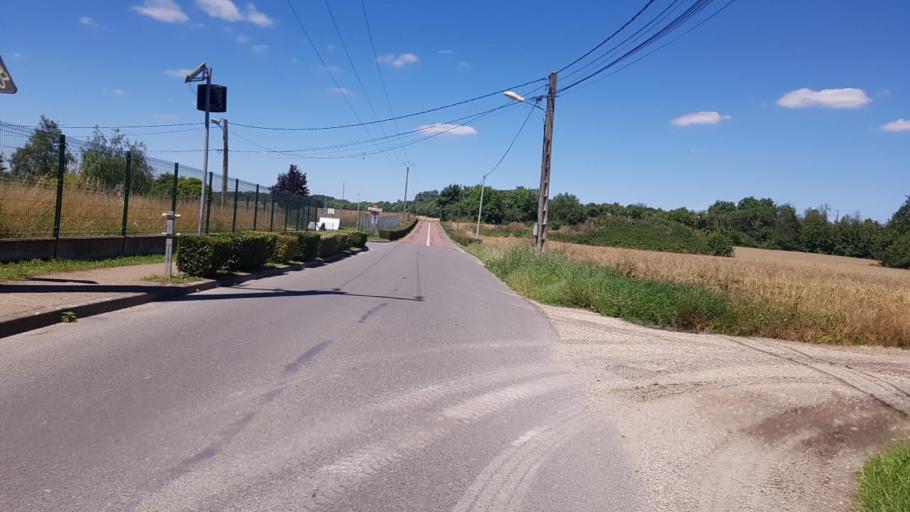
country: FR
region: Ile-de-France
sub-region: Departement de Seine-et-Marne
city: Sammeron
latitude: 48.9562
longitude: 3.0657
